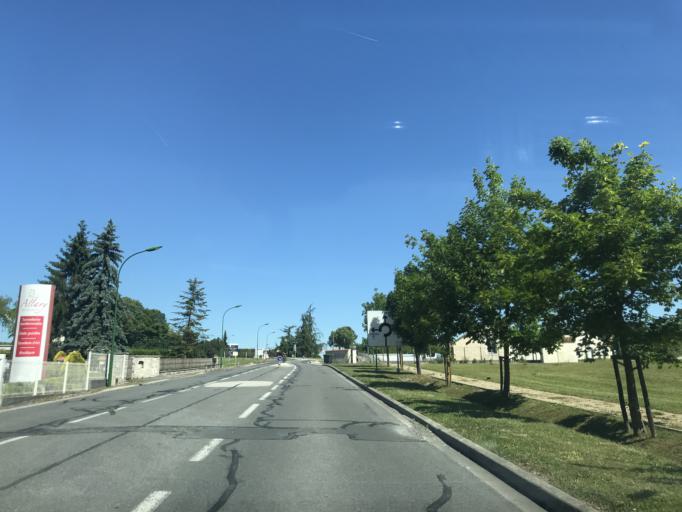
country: FR
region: Poitou-Charentes
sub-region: Departement de la Charente
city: Segonzac
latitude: 45.5272
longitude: -0.3036
